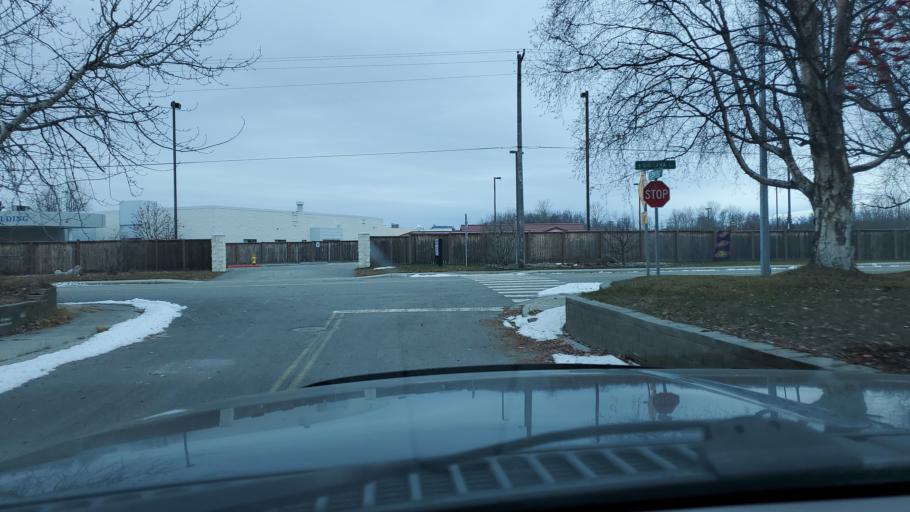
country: US
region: Alaska
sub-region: Matanuska-Susitna Borough
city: Palmer
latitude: 61.6021
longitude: -149.1025
